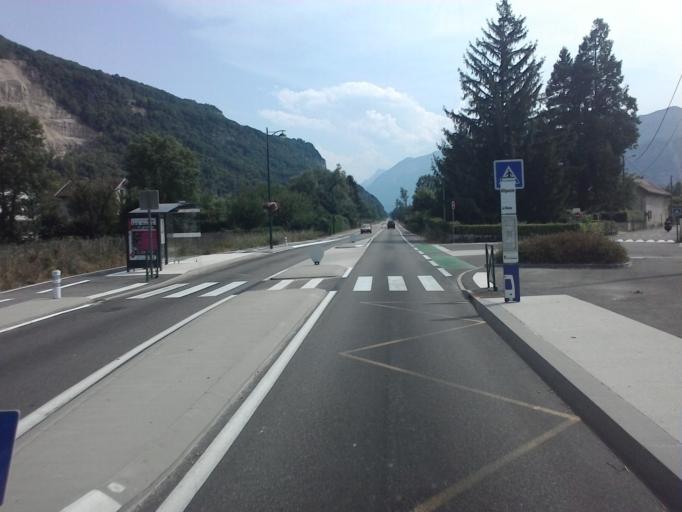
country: FR
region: Rhone-Alpes
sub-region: Departement de l'Isere
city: La Buisse
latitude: 45.3307
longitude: 5.6210
